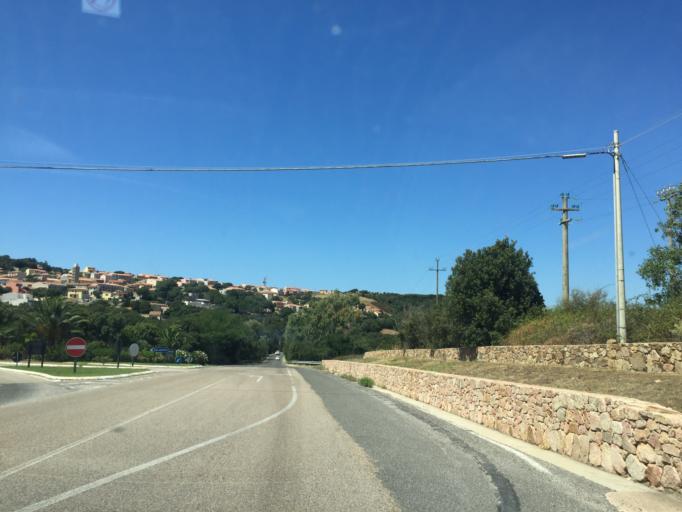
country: IT
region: Sardinia
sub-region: Provincia di Olbia-Tempio
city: Aglientu
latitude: 41.0747
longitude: 9.1179
